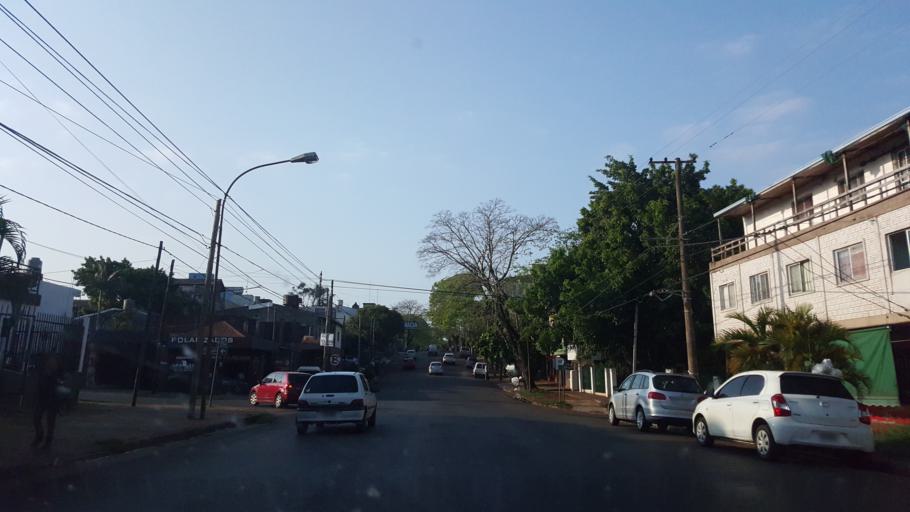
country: AR
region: Misiones
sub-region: Departamento de Capital
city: Posadas
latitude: -27.3795
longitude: -55.8955
